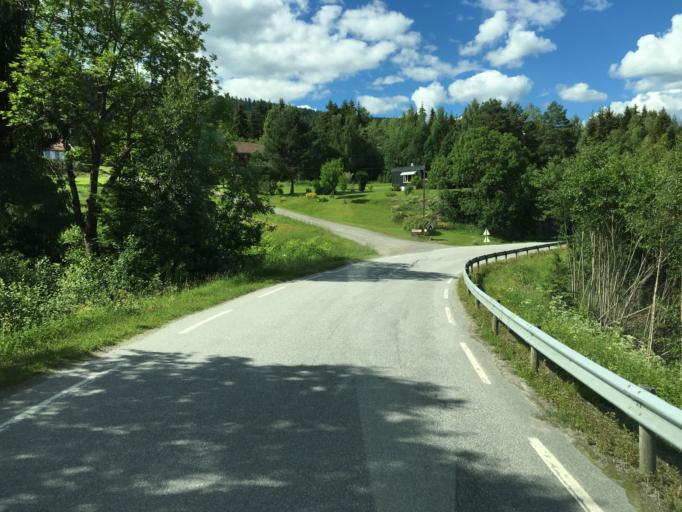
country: NO
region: Oppland
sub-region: Sondre Land
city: Hov
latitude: 60.5488
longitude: 10.2928
